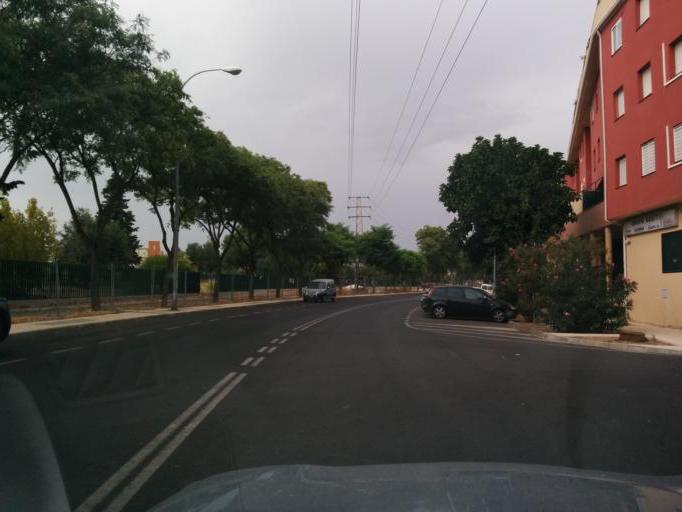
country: ES
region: Andalusia
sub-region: Provincia de Sevilla
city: Sevilla
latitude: 37.4021
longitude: -5.9317
